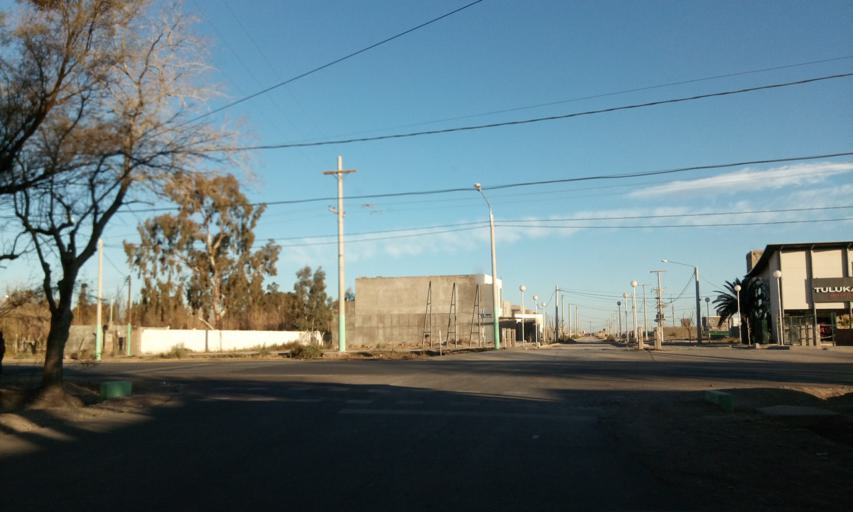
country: AR
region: San Juan
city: San Juan
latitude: -31.5385
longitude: -68.5898
